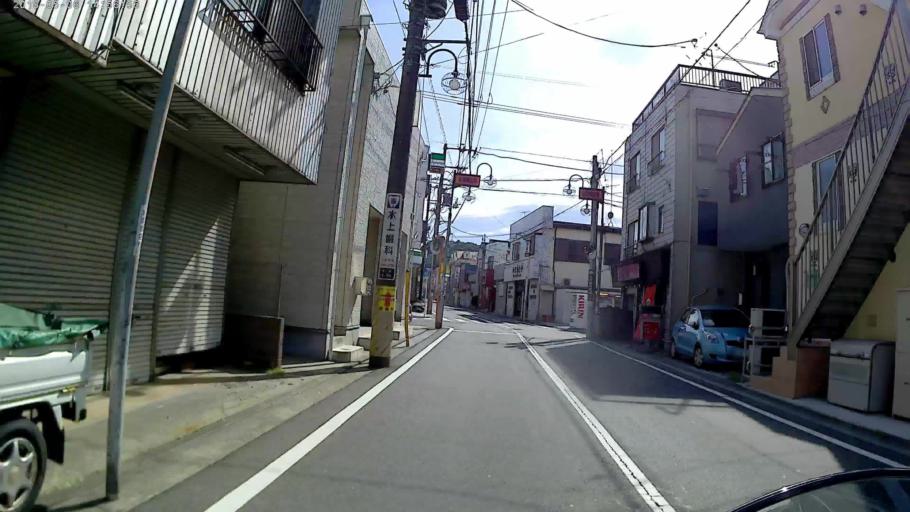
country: JP
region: Kanagawa
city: Yokohama
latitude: 35.4192
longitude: 139.6199
